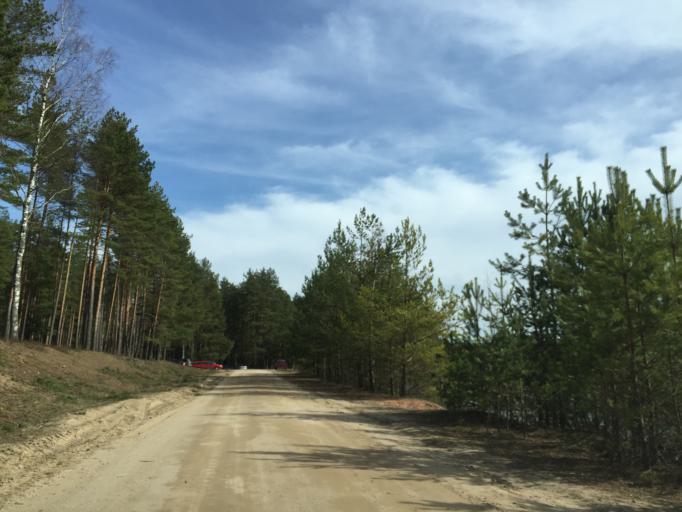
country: LV
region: Ikskile
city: Ikskile
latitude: 56.8414
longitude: 24.5514
